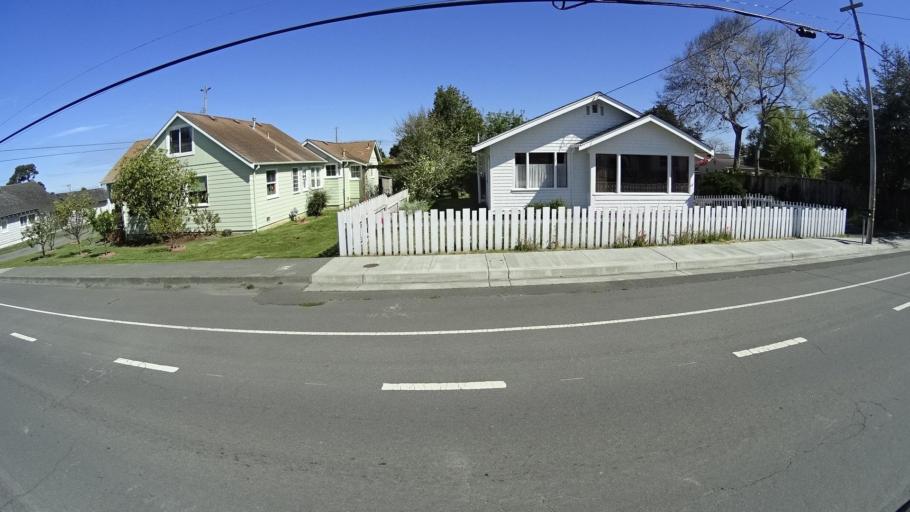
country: US
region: California
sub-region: Humboldt County
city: Myrtletown
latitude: 40.7951
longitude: -124.1335
